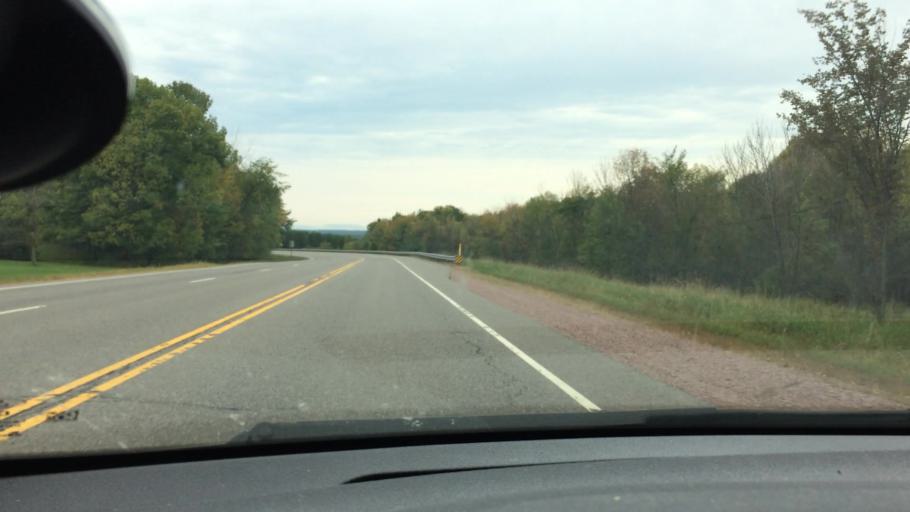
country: US
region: Wisconsin
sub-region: Clark County
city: Neillsville
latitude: 44.5654
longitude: -90.6613
